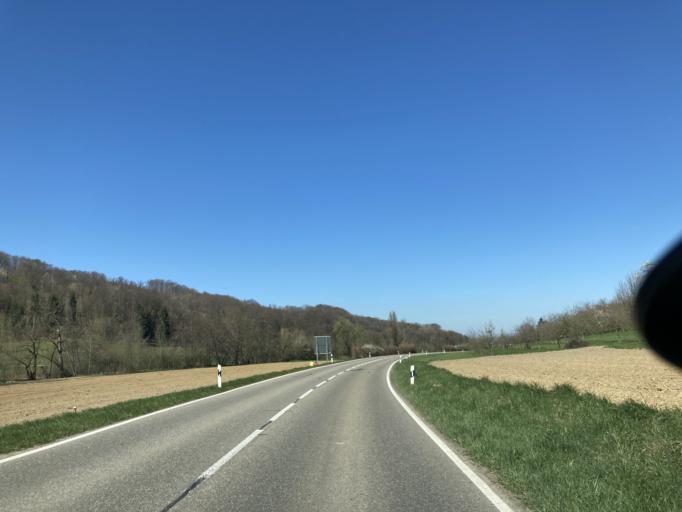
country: DE
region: Baden-Wuerttemberg
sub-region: Freiburg Region
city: Schliengen
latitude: 47.7422
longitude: 7.5976
